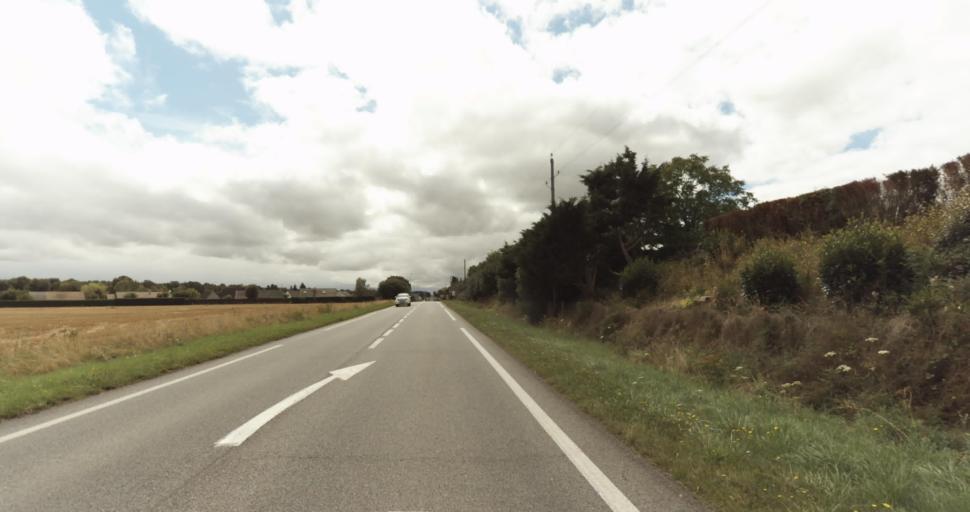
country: FR
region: Haute-Normandie
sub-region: Departement de l'Eure
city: Evreux
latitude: 48.9772
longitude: 1.1585
